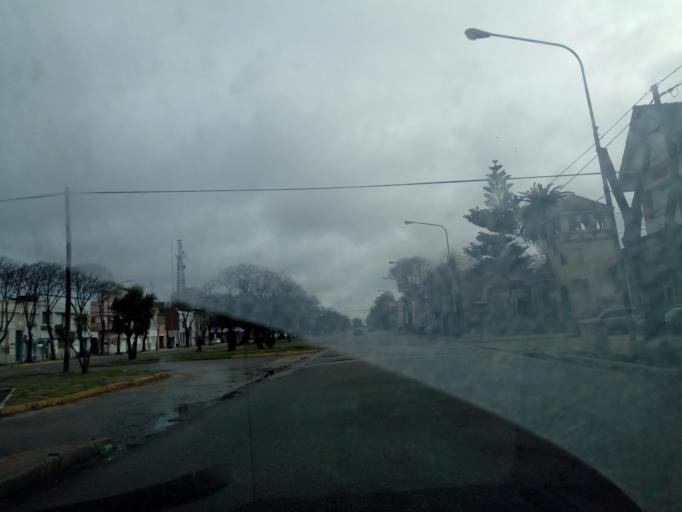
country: AR
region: Buenos Aires
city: Necochea
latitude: -38.5578
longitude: -58.7348
